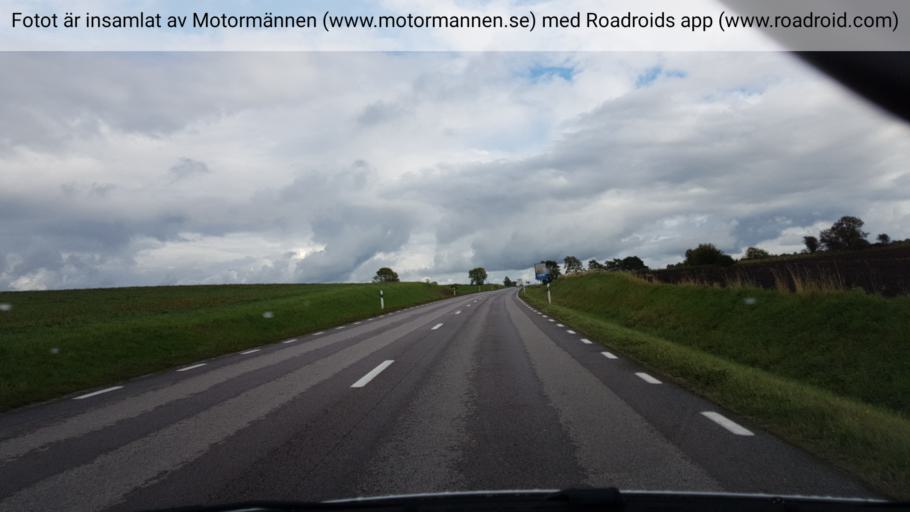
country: SE
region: Vaestra Goetaland
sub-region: Falkopings Kommun
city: Falkoeping
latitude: 58.1526
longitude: 13.5993
